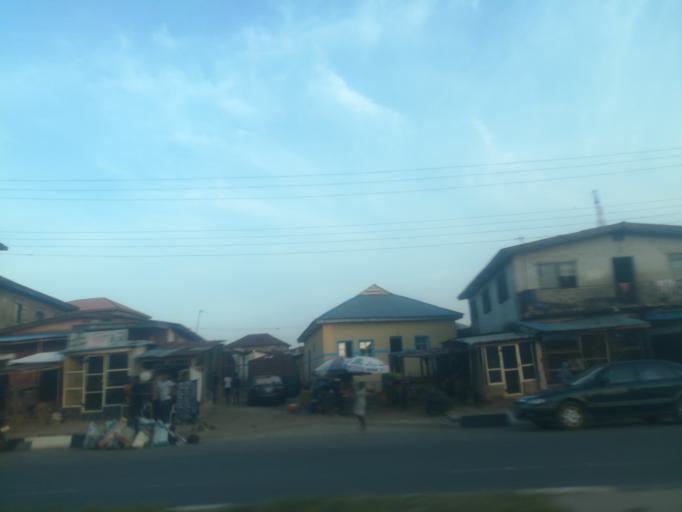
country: NG
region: Ogun
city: Abeokuta
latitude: 7.1505
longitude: 3.3299
